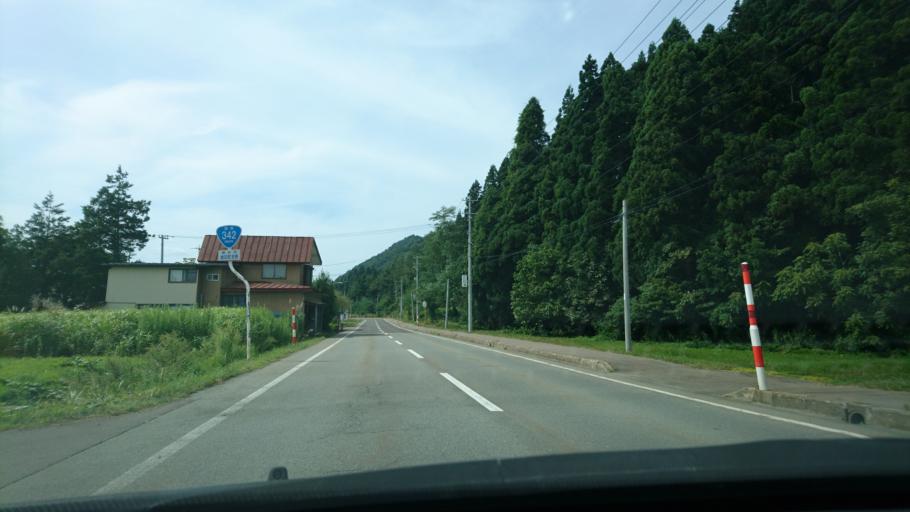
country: JP
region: Akita
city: Yuzawa
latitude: 39.1997
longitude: 140.6010
